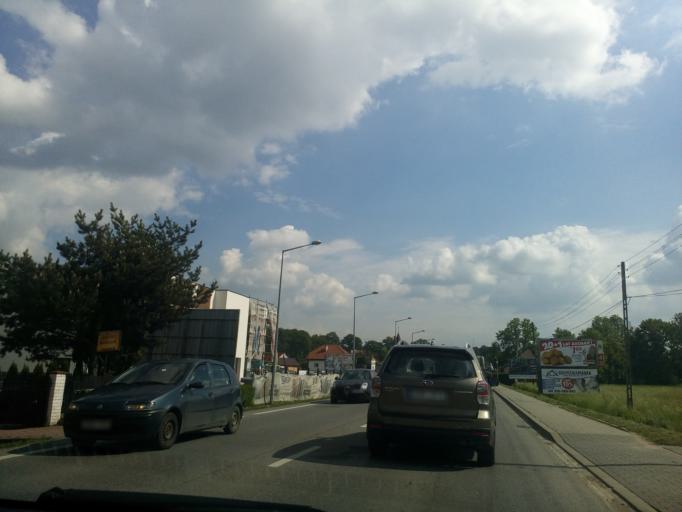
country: PL
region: Lesser Poland Voivodeship
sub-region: Powiat nowosadecki
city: Nowy Sacz
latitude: 49.6525
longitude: 20.6901
